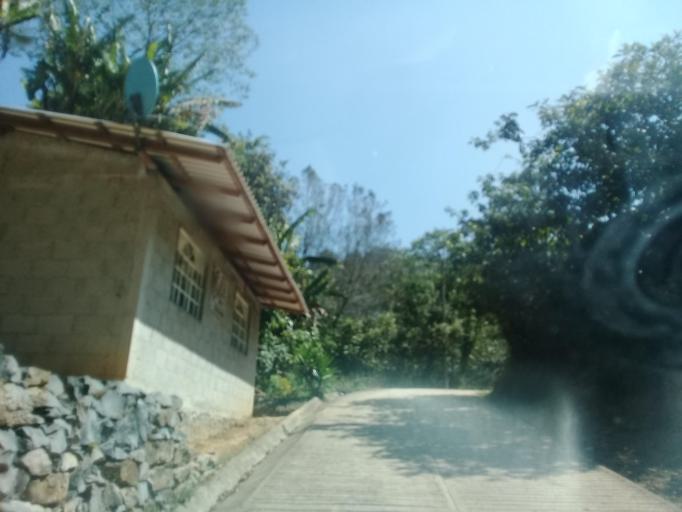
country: MX
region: Veracruz
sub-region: Tlilapan
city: Tonalixco
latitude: 18.7575
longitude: -97.0385
